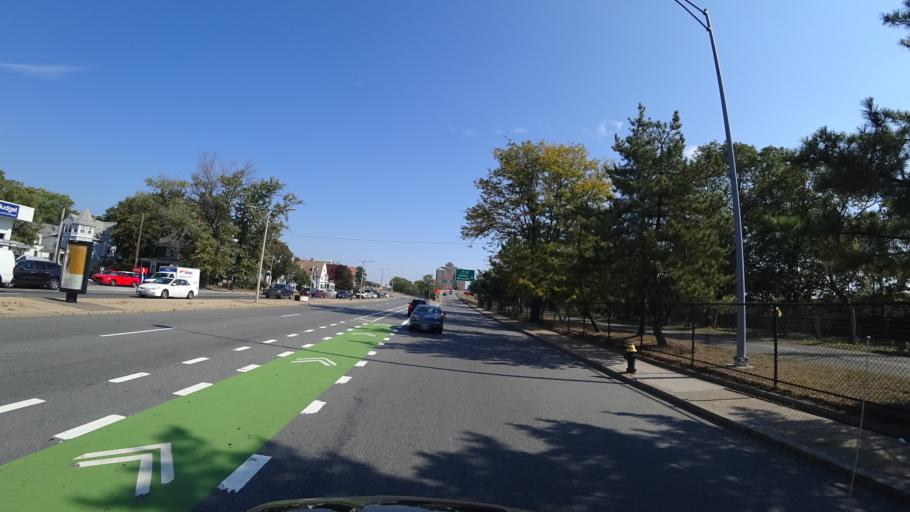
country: US
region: Massachusetts
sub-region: Middlesex County
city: Cambridge
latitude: 42.3582
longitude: -71.1252
